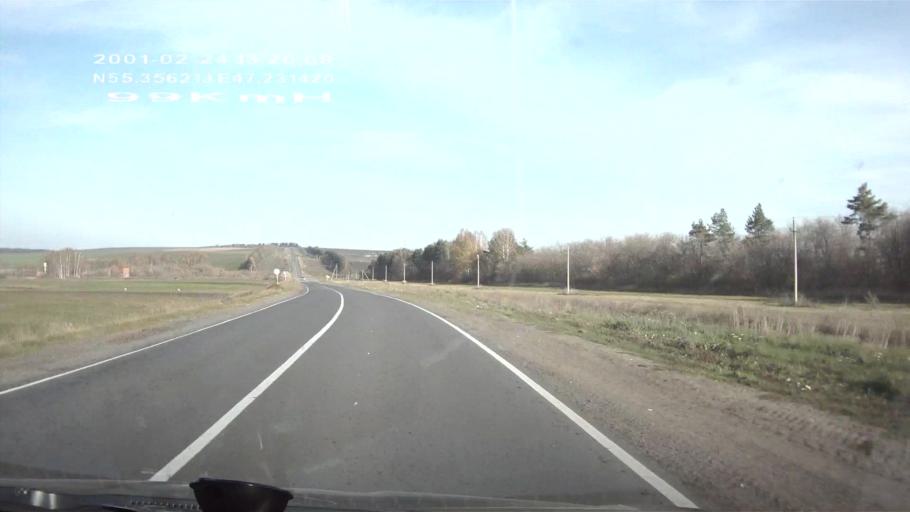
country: RU
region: Chuvashia
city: Ibresi
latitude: 55.3563
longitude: 47.2315
